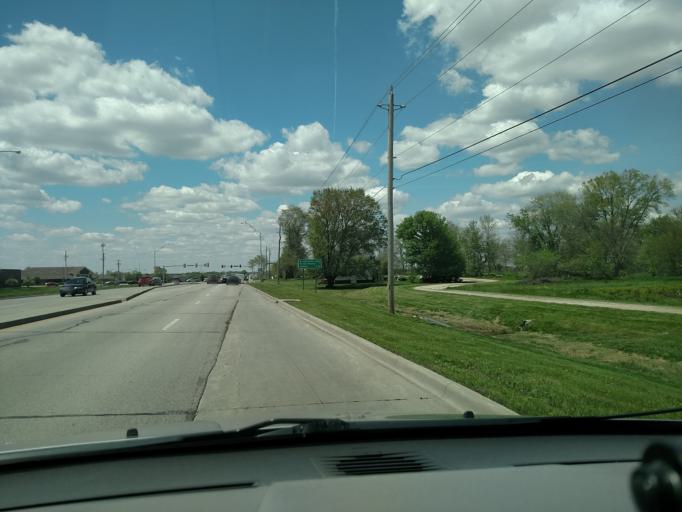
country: US
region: Iowa
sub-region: Polk County
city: Ankeny
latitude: 41.7029
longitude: -93.5980
